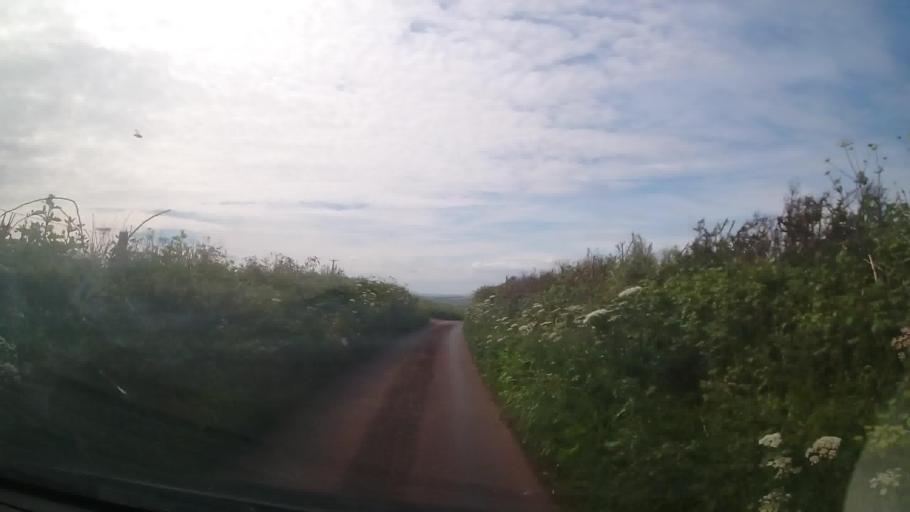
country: GB
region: England
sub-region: Devon
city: Salcombe
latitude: 50.2299
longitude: -3.6672
